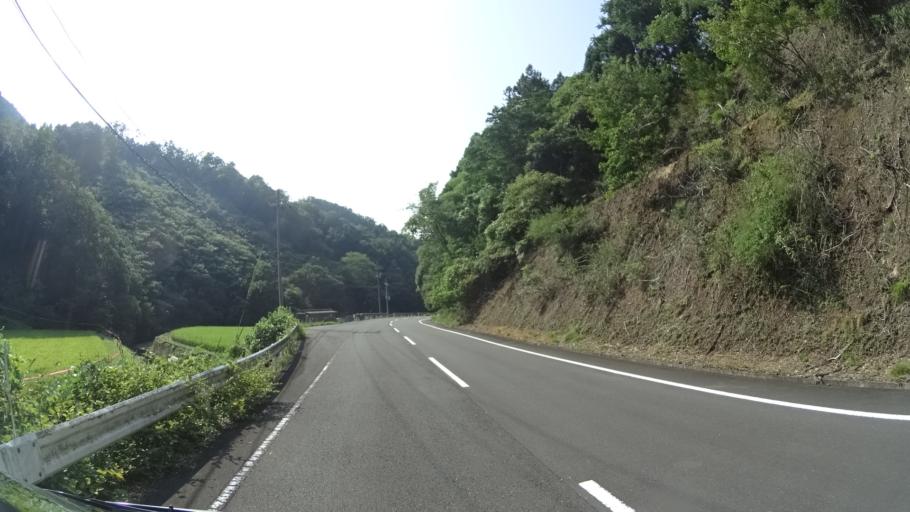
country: JP
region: Kyoto
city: Maizuru
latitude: 35.4173
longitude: 135.2279
